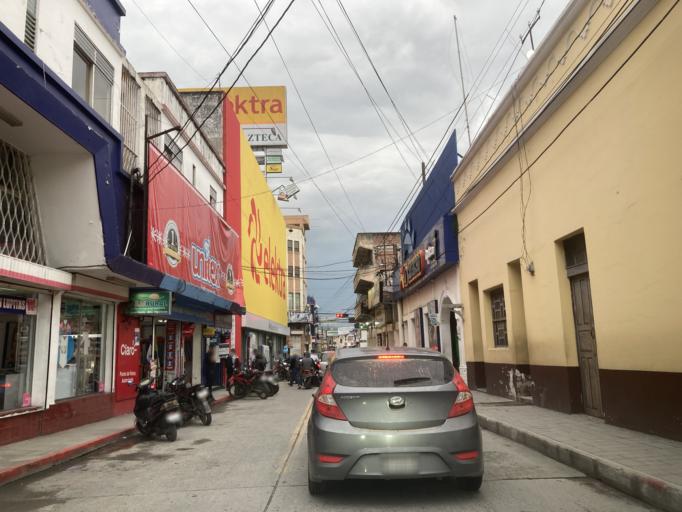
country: GT
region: Huehuetenango
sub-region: Municipio de Huehuetenango
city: Huehuetenango
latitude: 15.3208
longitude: -91.4705
